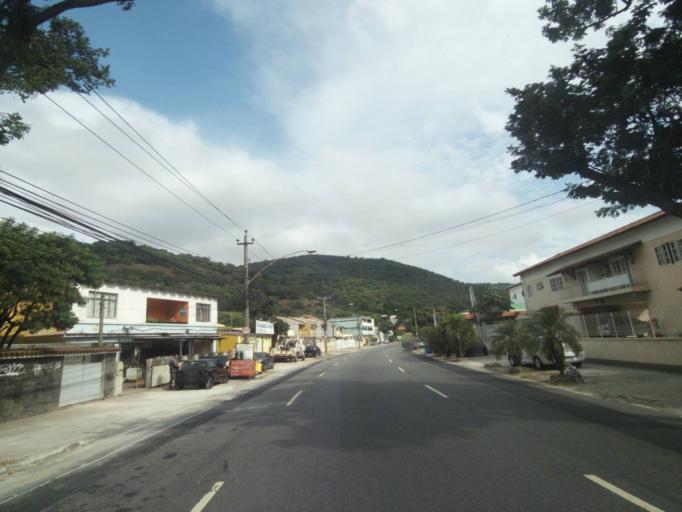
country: BR
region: Rio de Janeiro
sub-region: Nilopolis
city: Nilopolis
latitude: -22.8900
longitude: -43.3943
